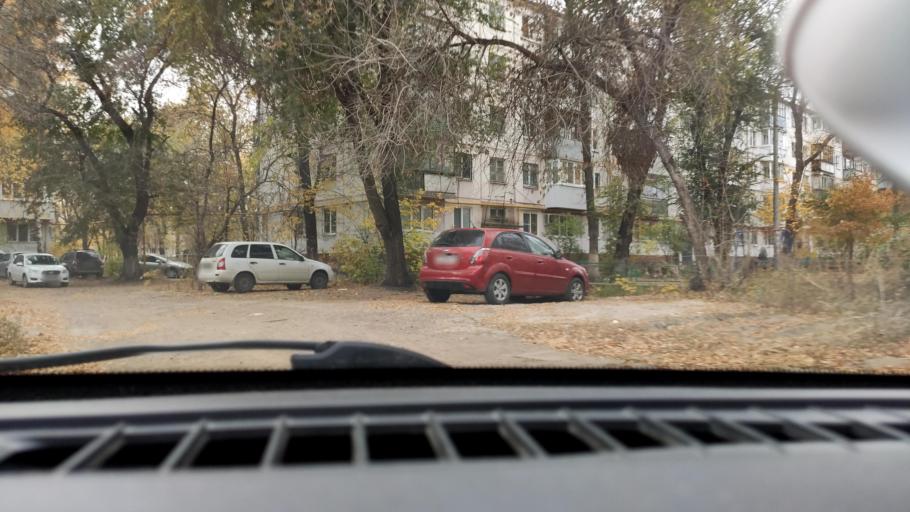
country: RU
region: Samara
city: Samara
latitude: 53.1950
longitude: 50.1966
